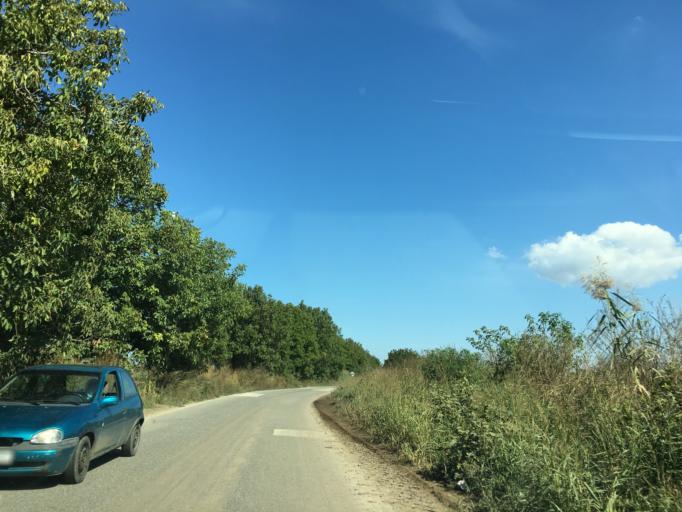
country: RO
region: Olt
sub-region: Comuna Orlea
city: Orlea
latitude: 43.6163
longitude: 24.3705
